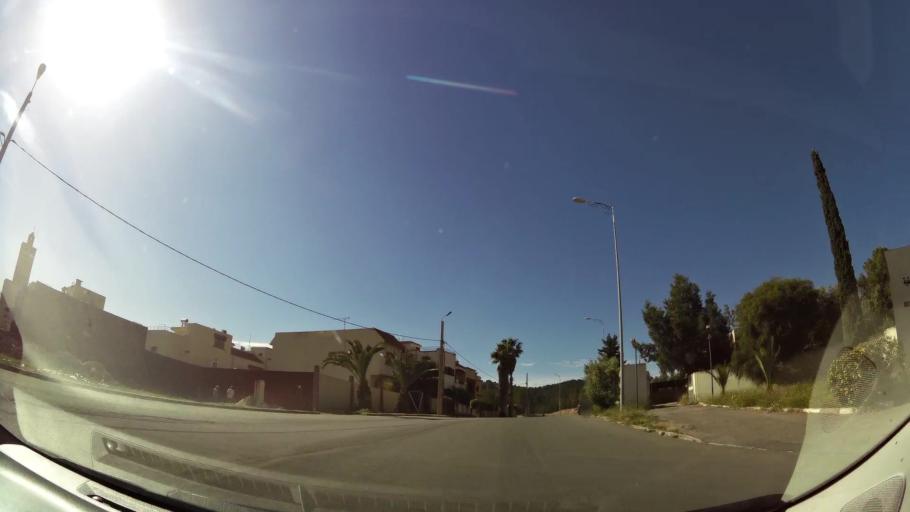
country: MA
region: Oriental
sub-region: Oujda-Angad
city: Oujda
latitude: 34.6486
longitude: -1.8935
